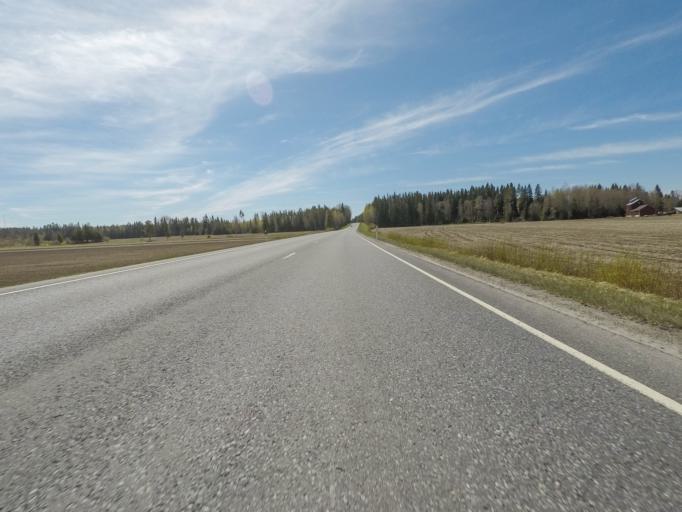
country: FI
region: Pirkanmaa
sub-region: Etelae-Pirkanmaa
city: Urjala
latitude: 61.0117
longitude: 23.4756
